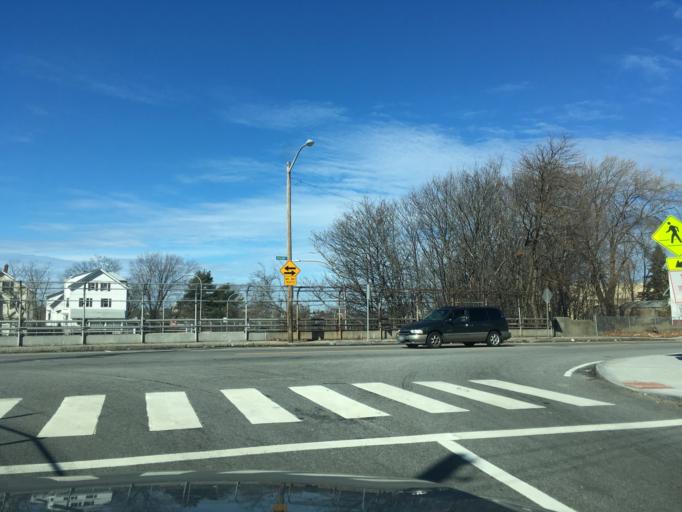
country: US
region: Rhode Island
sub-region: Providence County
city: Pawtucket
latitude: 41.8825
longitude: -71.3771
